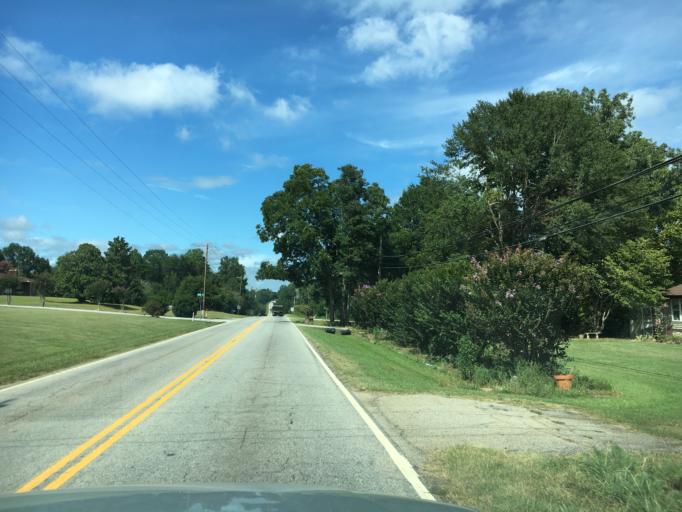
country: US
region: South Carolina
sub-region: Spartanburg County
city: Lyman
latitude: 34.9685
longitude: -82.1209
